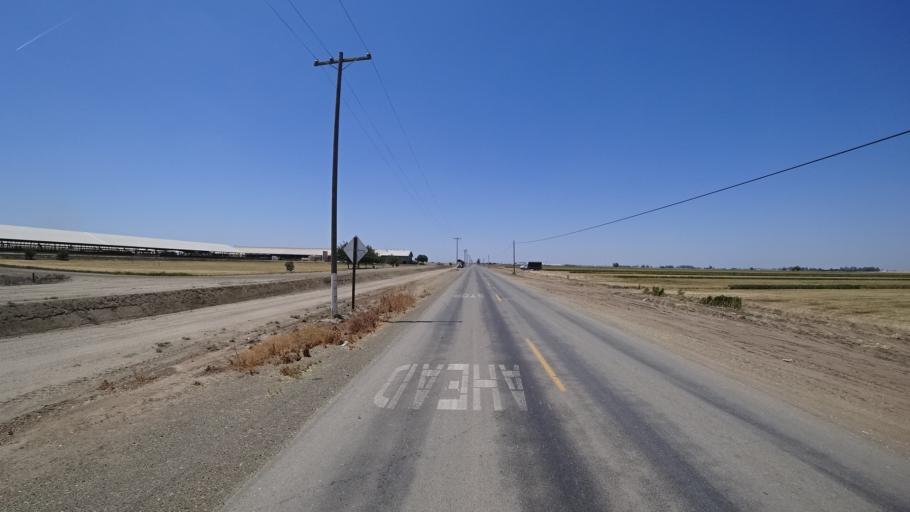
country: US
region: California
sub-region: Kings County
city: Corcoran
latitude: 36.1965
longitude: -119.6028
